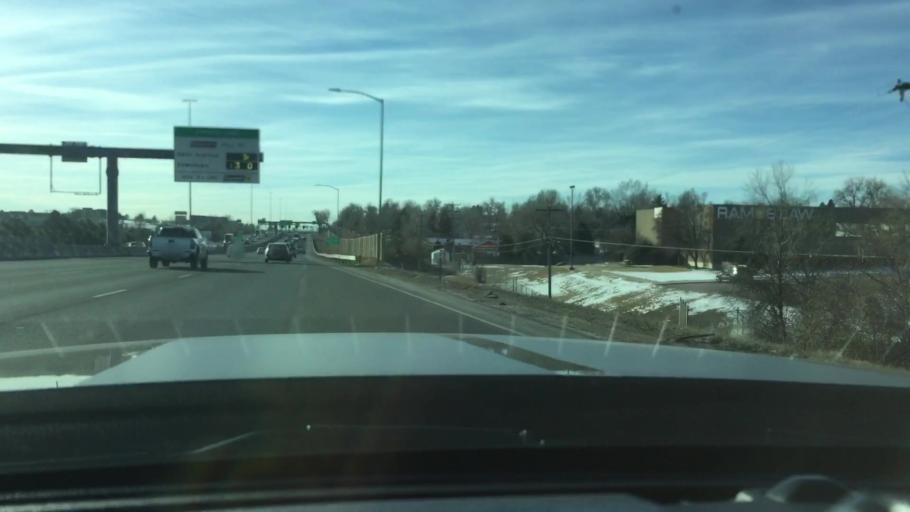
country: US
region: Colorado
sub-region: Adams County
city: Northglenn
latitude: 39.8817
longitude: -104.9878
